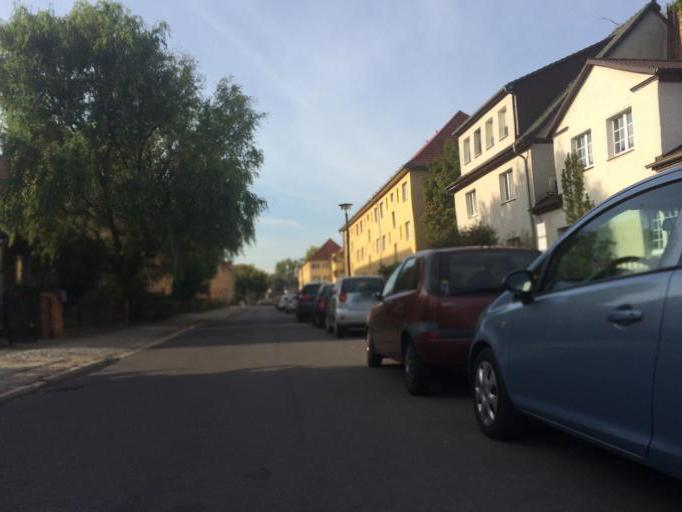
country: DE
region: Berlin
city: Alt-Hohenschoenhausen
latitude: 52.5524
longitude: 13.4963
